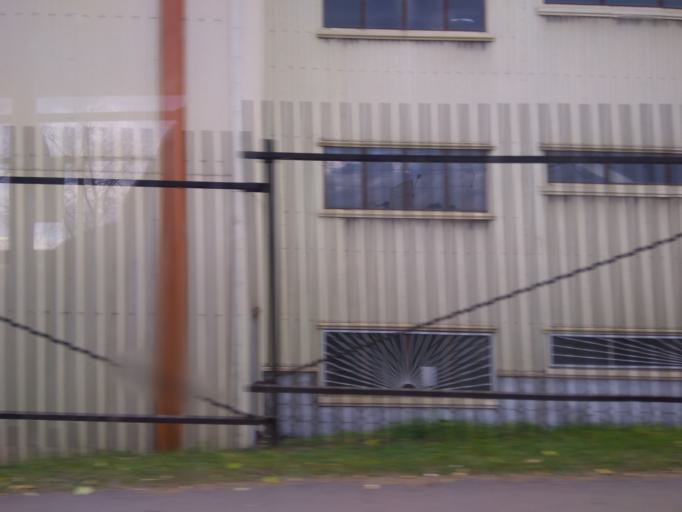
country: RU
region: Moskovskaya
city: Kozhukhovo
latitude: 55.7124
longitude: 37.6802
